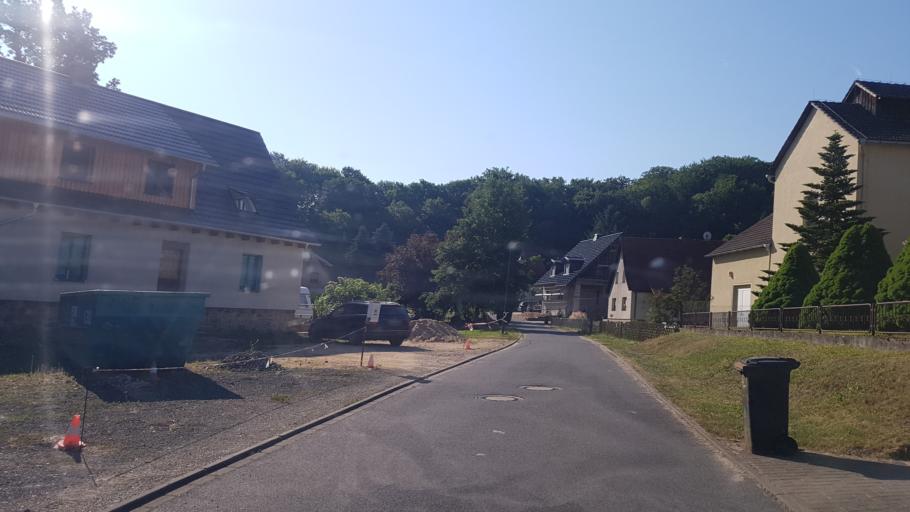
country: DE
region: Brandenburg
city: Lebusa
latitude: 51.7801
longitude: 13.3986
